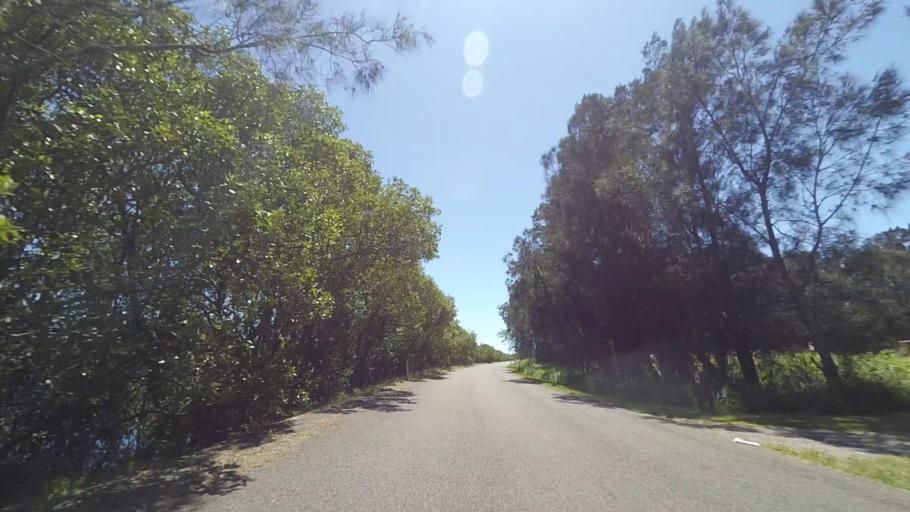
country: AU
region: New South Wales
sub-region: Port Stephens Shire
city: Medowie
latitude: -32.7825
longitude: 151.9429
